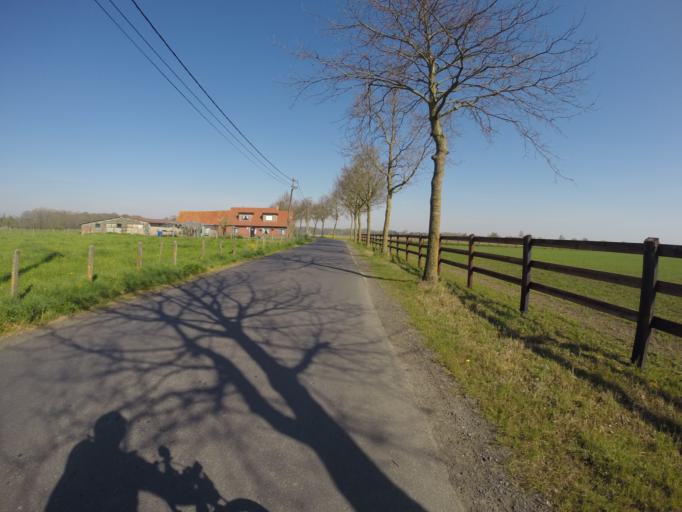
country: BE
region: Flanders
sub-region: Provincie Oost-Vlaanderen
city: Aalter
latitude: 51.0887
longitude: 3.4272
